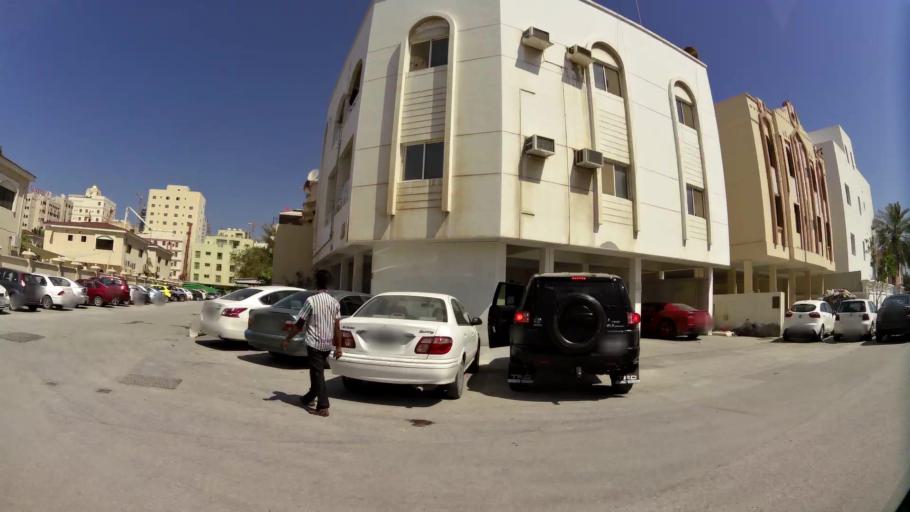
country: BH
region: Manama
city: Manama
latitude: 26.2097
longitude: 50.6114
